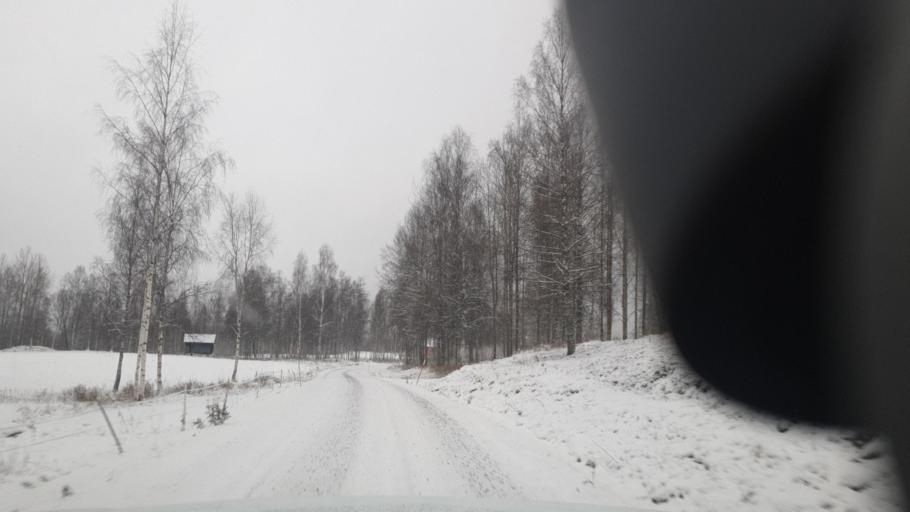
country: NO
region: Ostfold
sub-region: Romskog
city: Romskog
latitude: 59.8607
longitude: 11.9688
